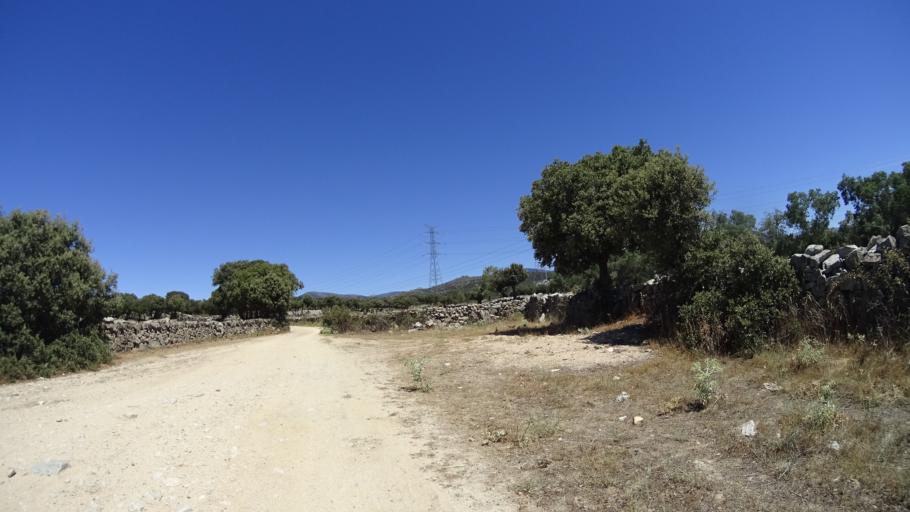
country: ES
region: Madrid
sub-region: Provincia de Madrid
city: Collado Mediano
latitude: 40.6772
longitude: -4.0391
